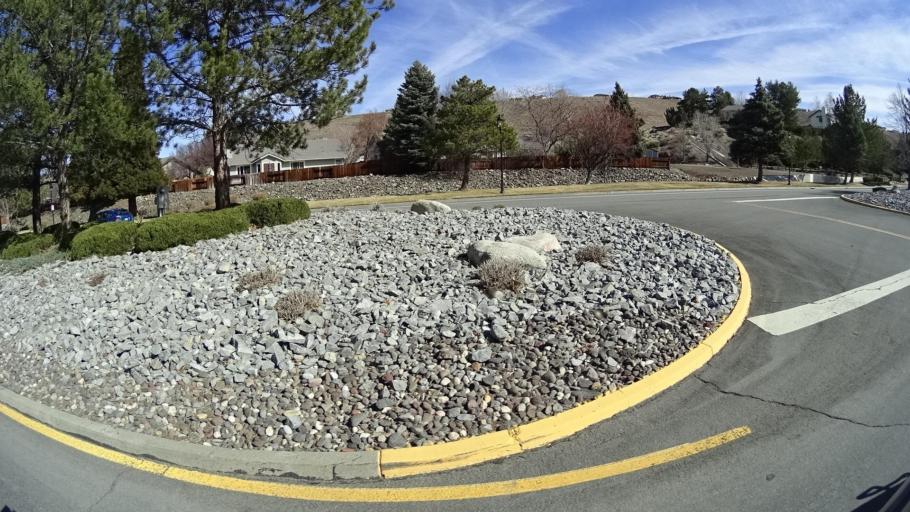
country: US
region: Nevada
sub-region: Washoe County
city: Spanish Springs
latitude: 39.5847
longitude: -119.7083
